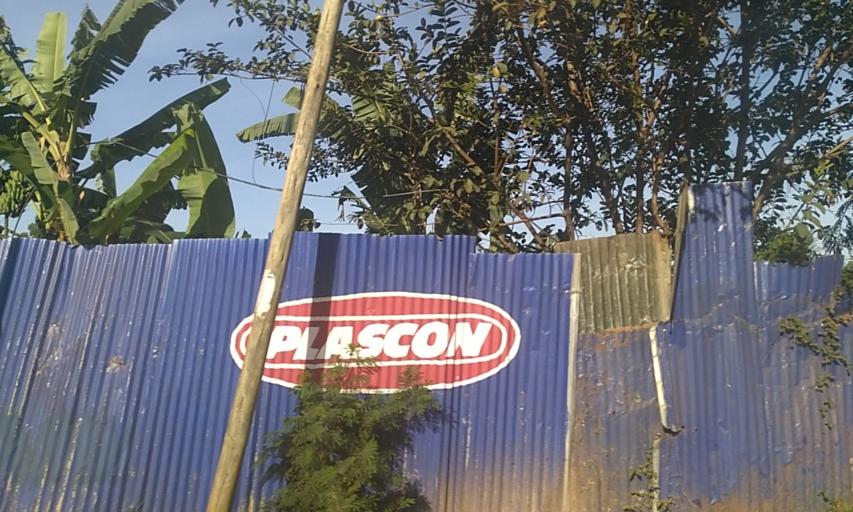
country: UG
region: Central Region
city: Kampala Central Division
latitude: 0.3399
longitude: 32.5966
